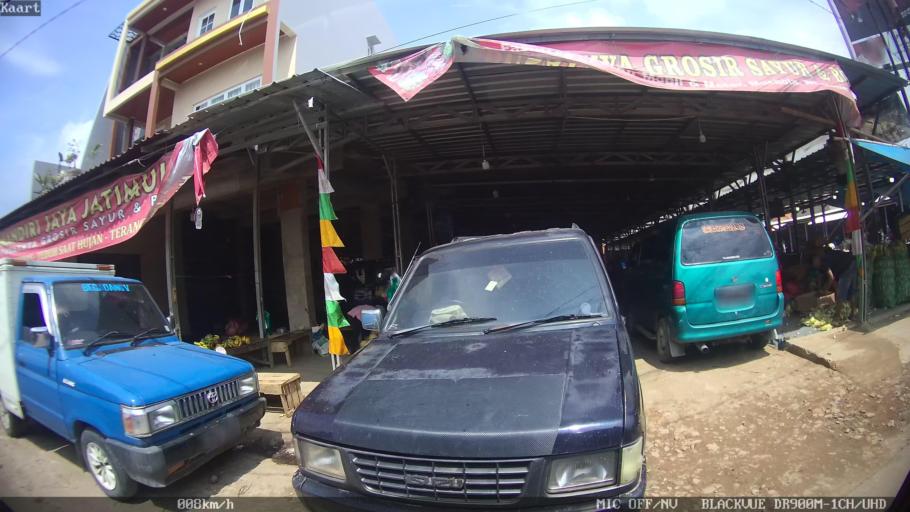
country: ID
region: Lampung
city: Kedaton
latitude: -5.3375
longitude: 105.2928
